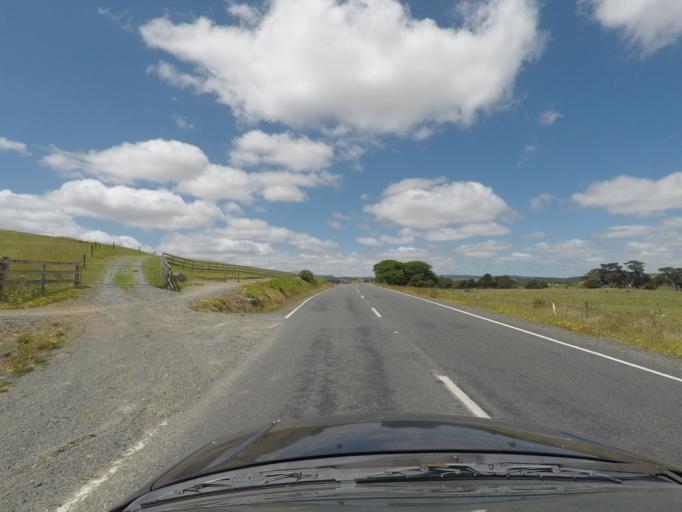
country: NZ
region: Northland
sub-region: Whangarei
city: Ruakaka
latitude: -35.9886
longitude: 174.4566
